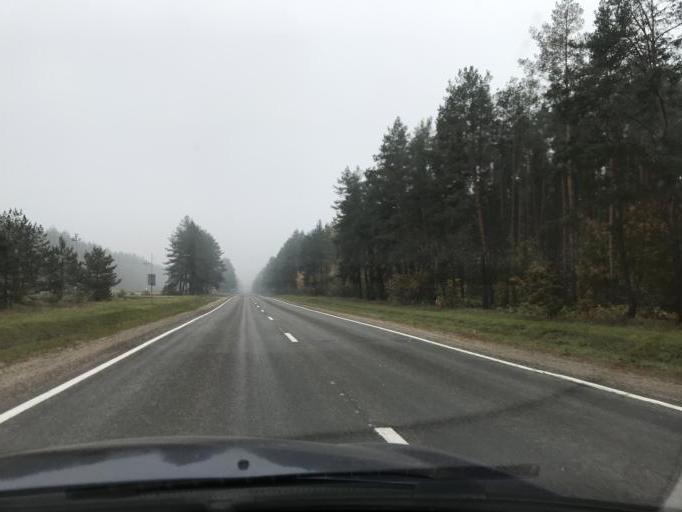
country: BY
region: Grodnenskaya
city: Hrodna
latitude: 53.8003
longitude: 23.8582
